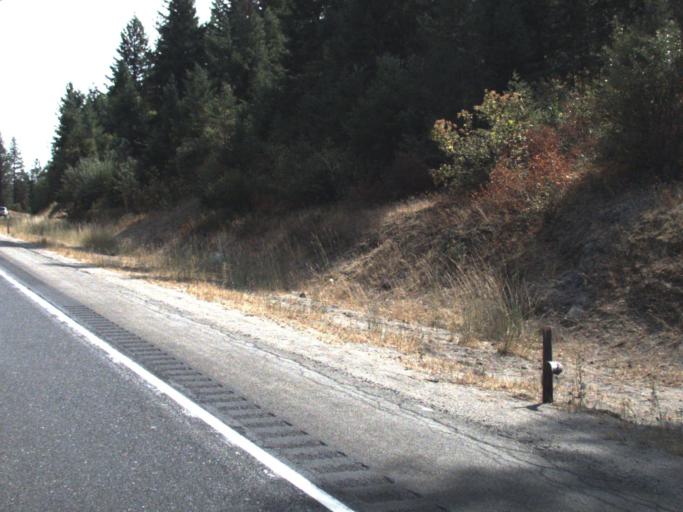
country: US
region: Washington
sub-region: Spokane County
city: Deer Park
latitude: 48.0282
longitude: -117.5973
